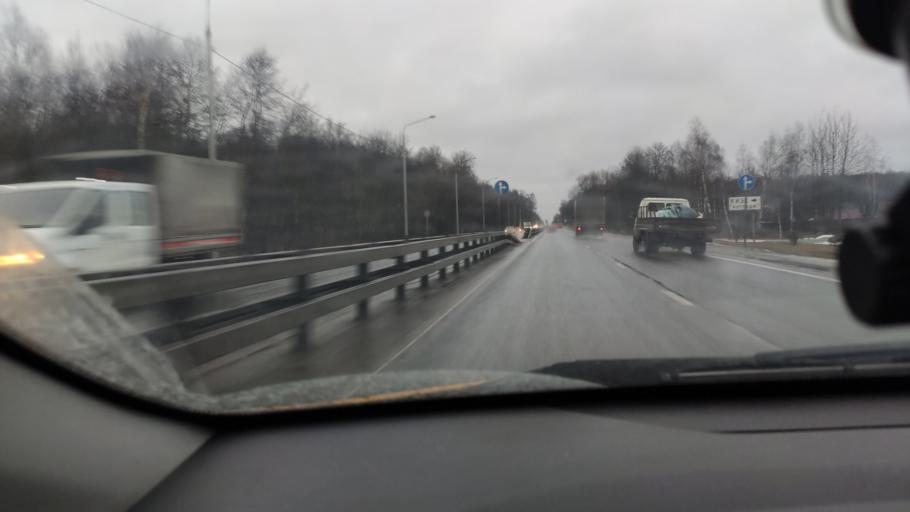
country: RU
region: Moskovskaya
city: Troitsk
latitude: 55.3561
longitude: 37.3493
